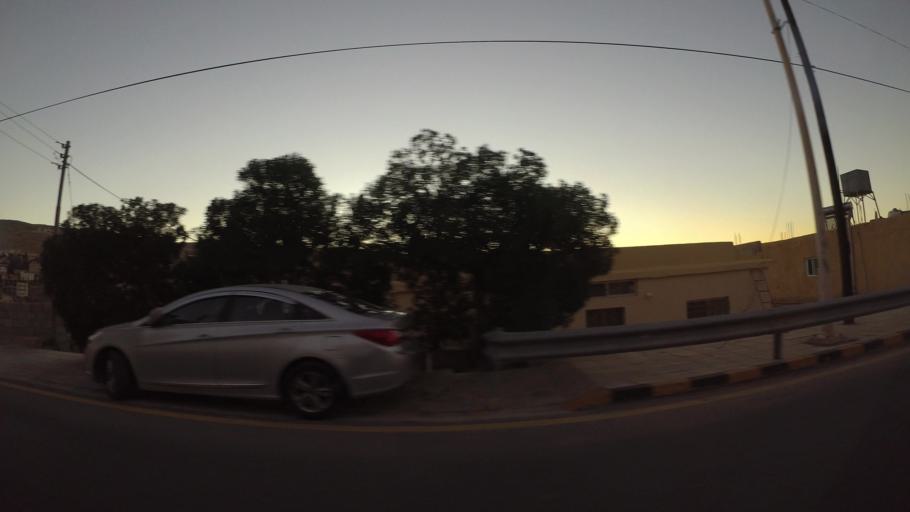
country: JO
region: Ma'an
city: Petra
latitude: 30.3158
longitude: 35.4824
